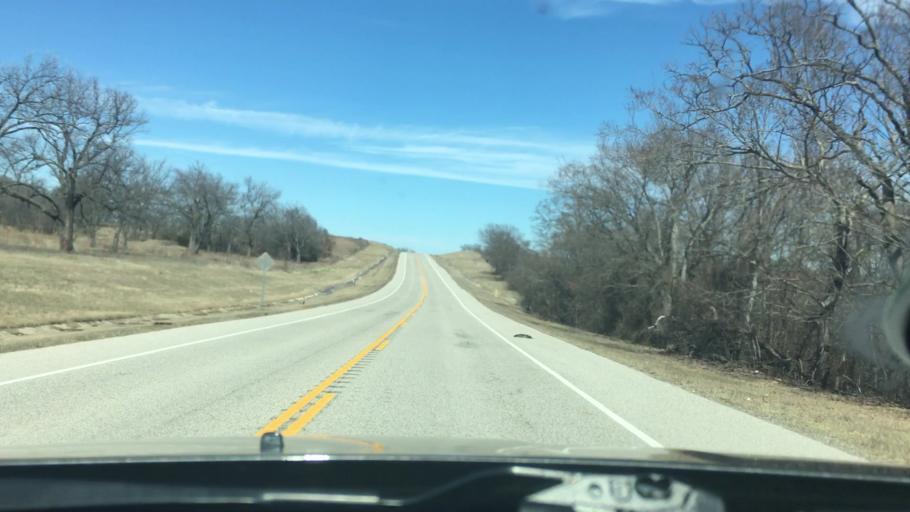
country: US
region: Oklahoma
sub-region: Carter County
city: Dickson
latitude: 34.3371
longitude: -96.9509
